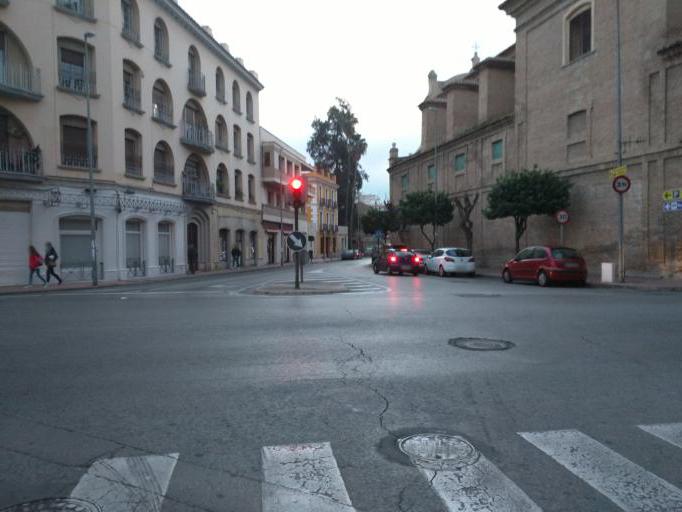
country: ES
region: Murcia
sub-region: Murcia
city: Murcia
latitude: 37.9882
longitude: -1.1385
